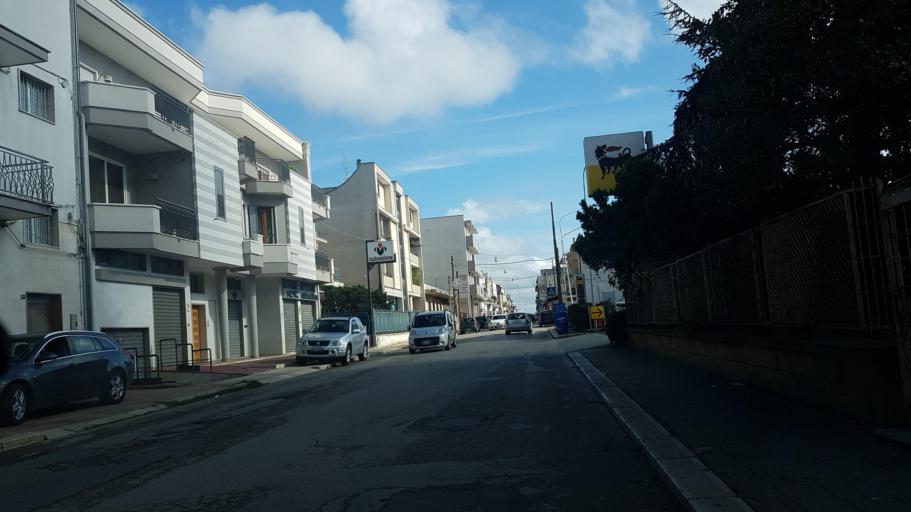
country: IT
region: Apulia
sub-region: Provincia di Brindisi
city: Carovigno
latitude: 40.7048
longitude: 17.6536
